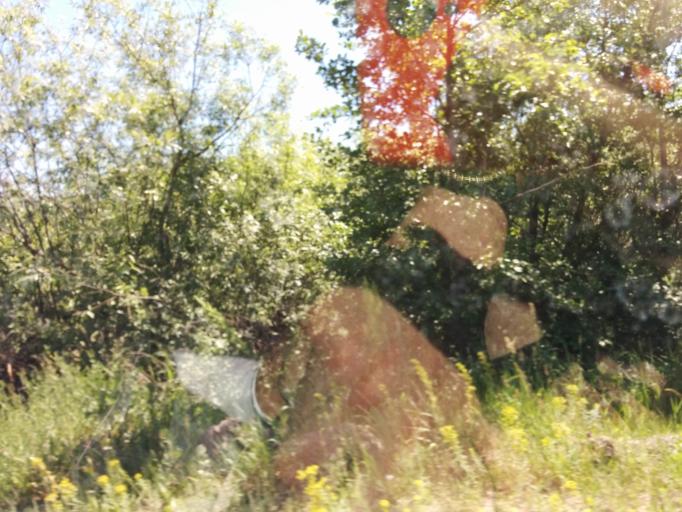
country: RU
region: Tambov
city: Morshansk
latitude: 53.6138
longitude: 41.8402
